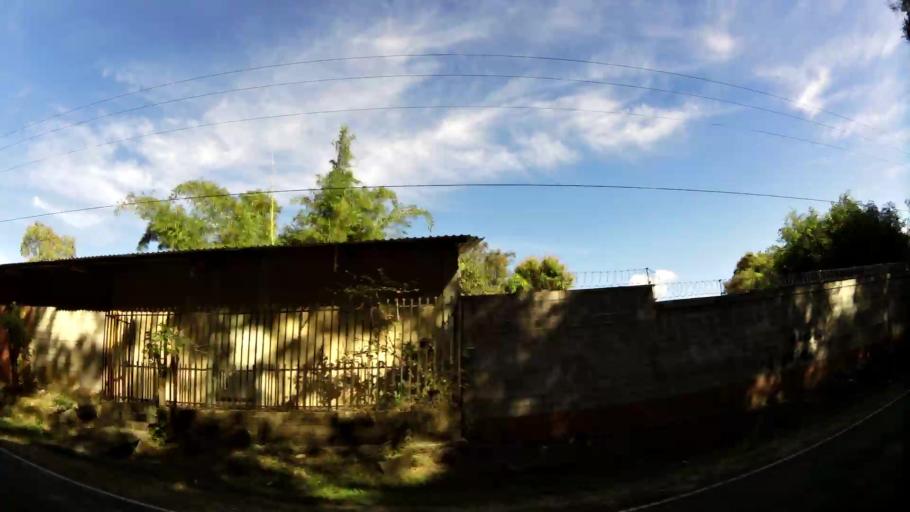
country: SV
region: Cuscatlan
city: Tenancingo
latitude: 13.8418
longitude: -89.0281
